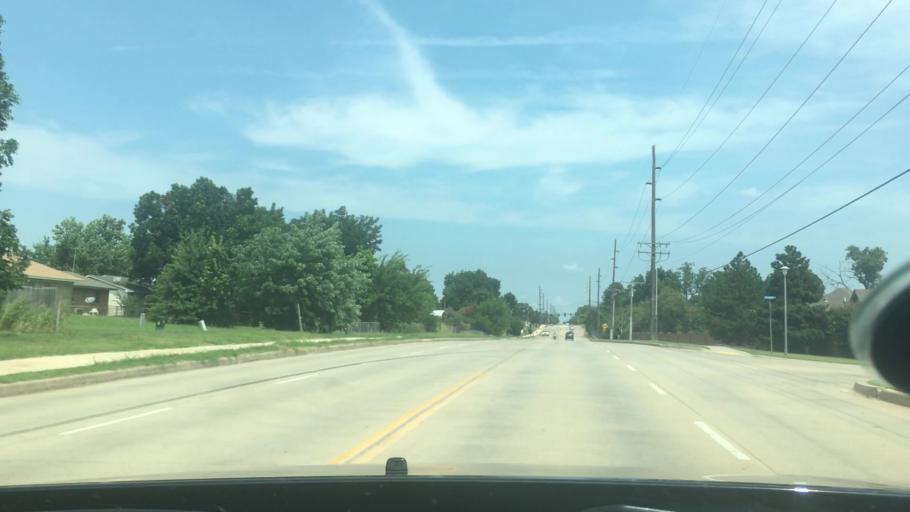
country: US
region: Oklahoma
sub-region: Pottawatomie County
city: Shawnee
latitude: 35.3430
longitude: -96.8943
